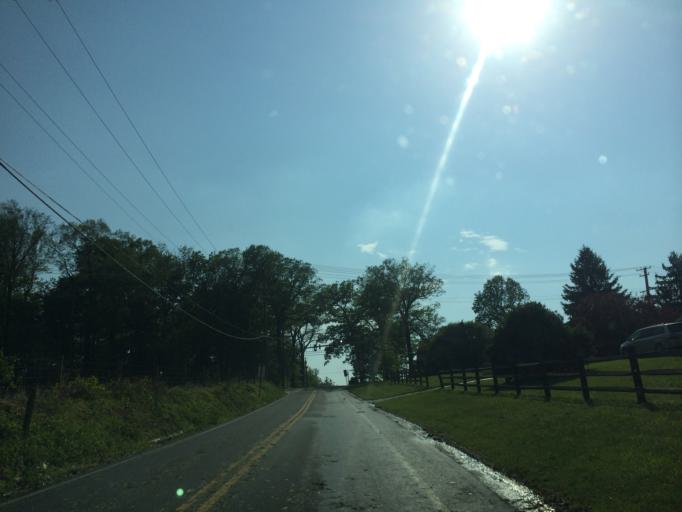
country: US
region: Maryland
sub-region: Howard County
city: Highland
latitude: 39.1728
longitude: -76.9511
